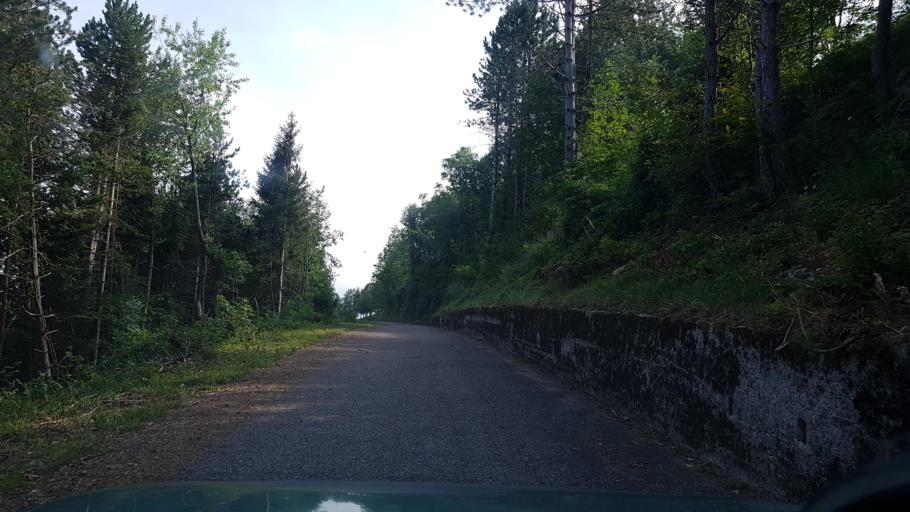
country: IT
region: Friuli Venezia Giulia
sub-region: Provincia di Udine
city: Torreano
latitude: 46.1716
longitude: 13.4135
